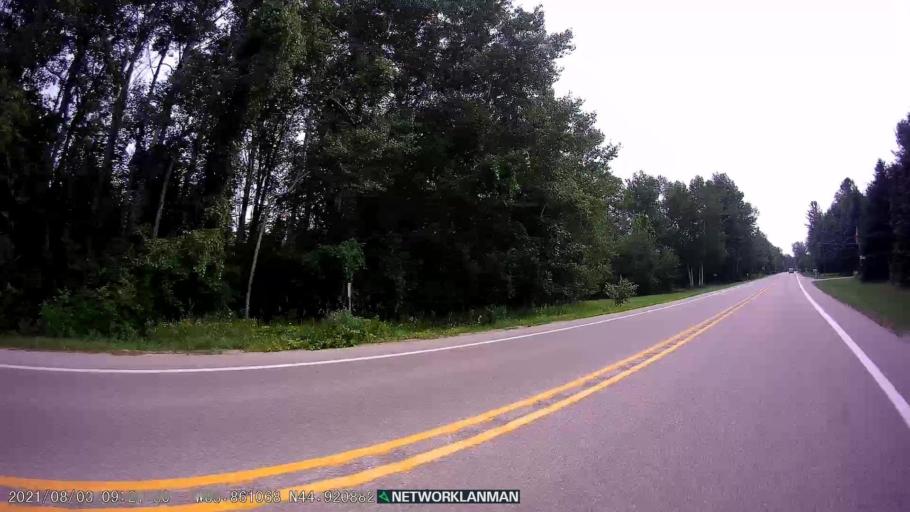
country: US
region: Michigan
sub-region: Leelanau County
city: Leland
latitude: 44.9208
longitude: -85.8608
